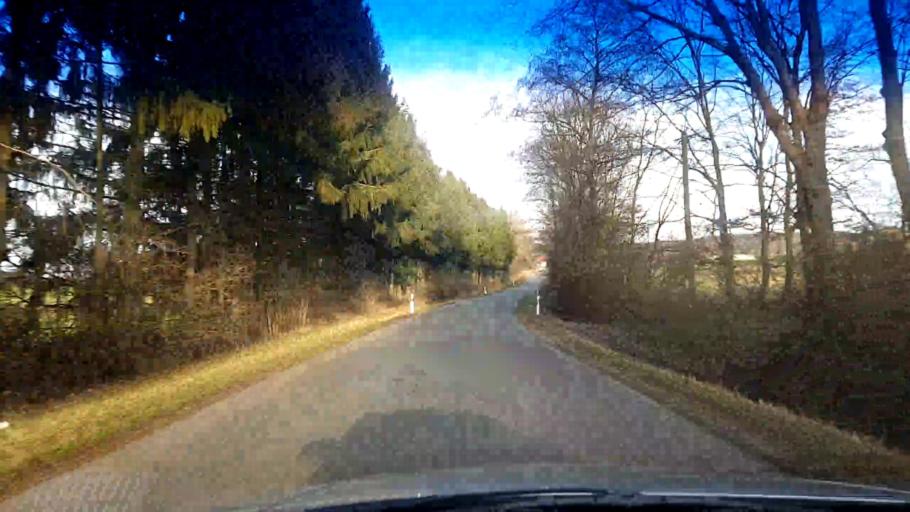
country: DE
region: Bavaria
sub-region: Upper Franconia
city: Hirschaid
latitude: 49.8264
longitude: 11.0000
